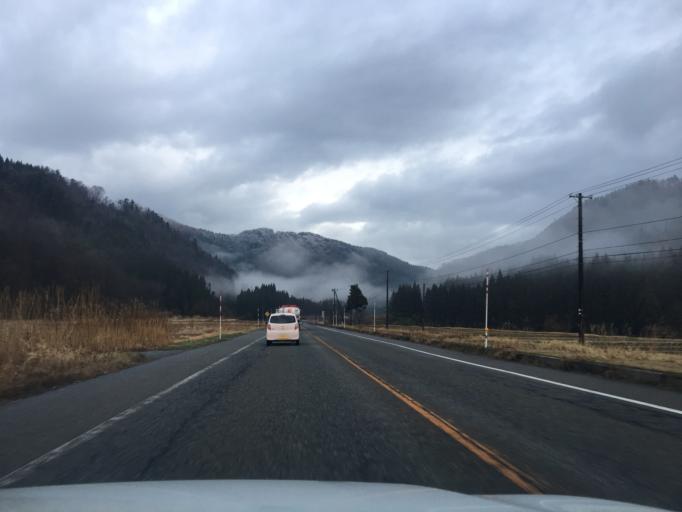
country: JP
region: Niigata
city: Murakami
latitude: 38.4443
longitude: 139.5845
